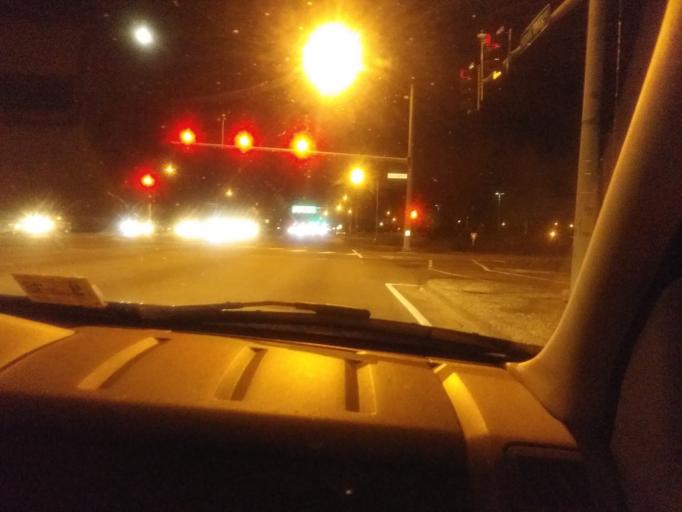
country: US
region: Virginia
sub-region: City of Chesapeake
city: Chesapeake
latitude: 36.8045
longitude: -76.1900
